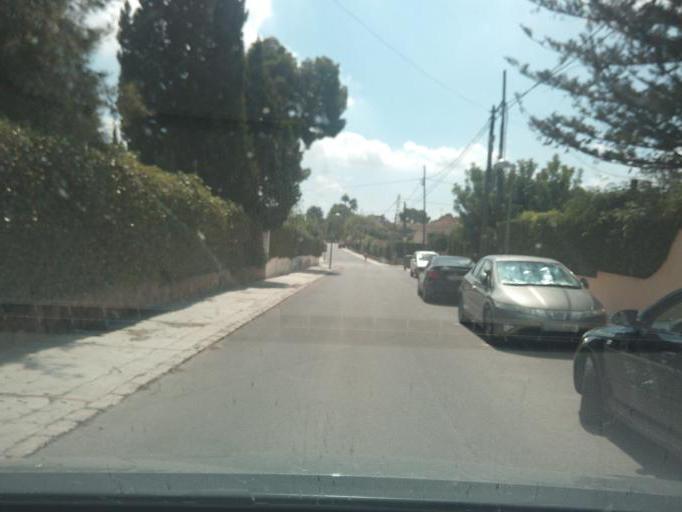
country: ES
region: Valencia
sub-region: Provincia de Valencia
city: Manises
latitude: 39.5400
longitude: -0.4862
